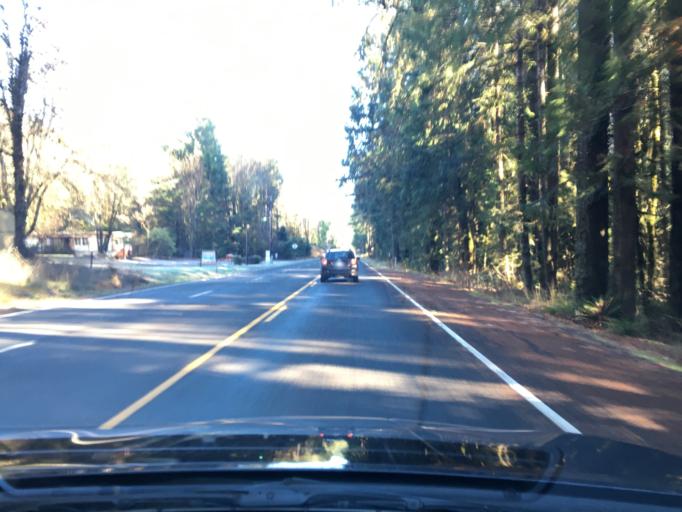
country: US
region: Oregon
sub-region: Douglas County
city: Glide
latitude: 43.2970
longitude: -122.9136
